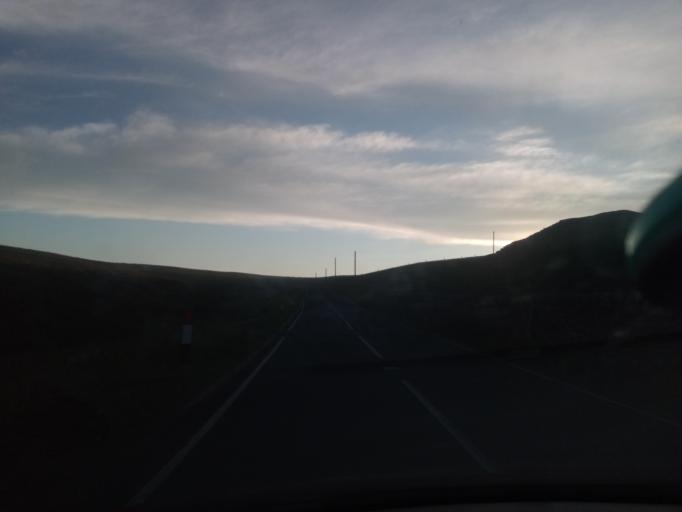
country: GB
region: England
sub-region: Northumberland
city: Bardon Mill
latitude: 54.7846
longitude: -2.2838
